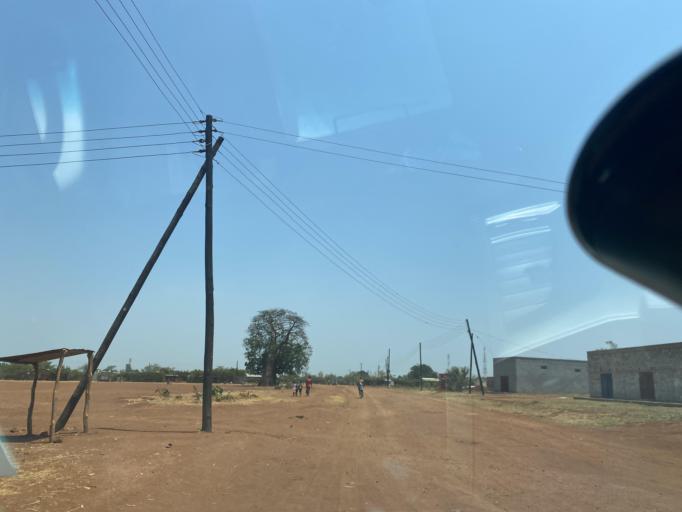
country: ZM
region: Southern
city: Nakambala
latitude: -15.5150
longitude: 27.9330
